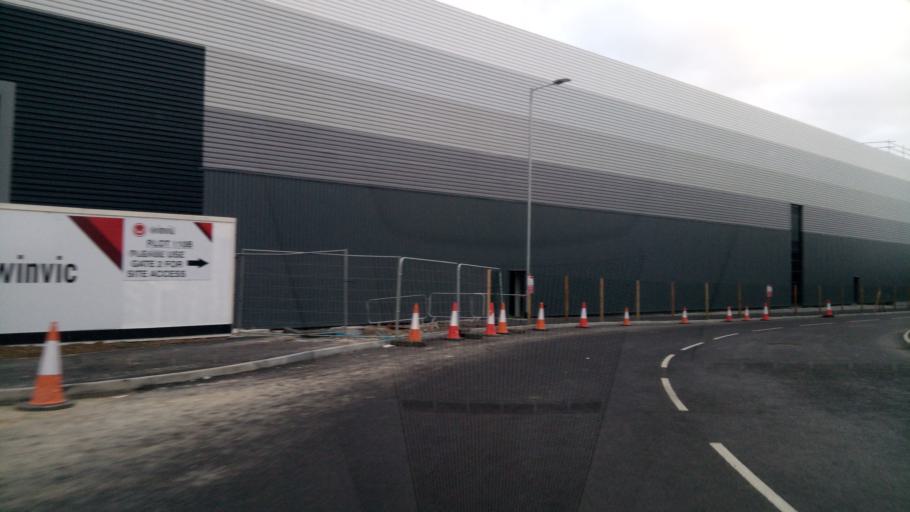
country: GB
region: England
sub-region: Cambridgeshire
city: Yaxley
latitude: 52.5337
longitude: -0.2999
